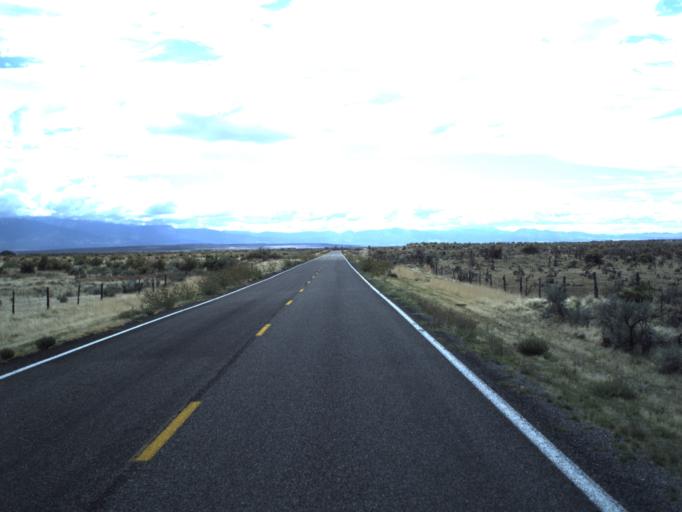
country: US
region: Utah
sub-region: Millard County
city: Fillmore
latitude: 39.1524
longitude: -112.4099
